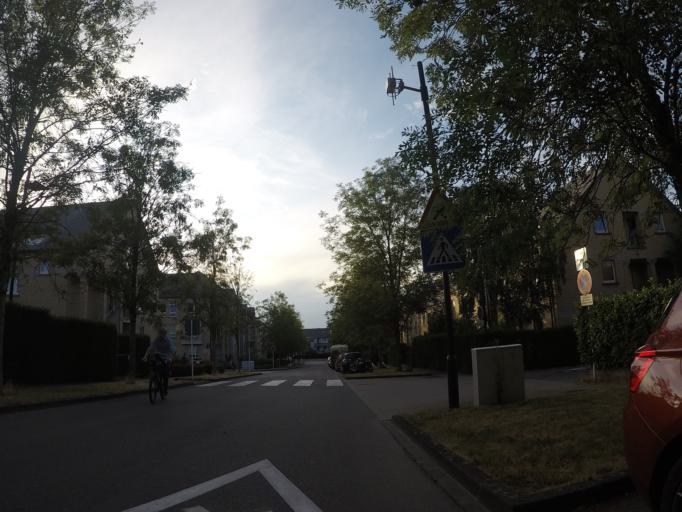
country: LU
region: Luxembourg
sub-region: Canton de Luxembourg
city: Luxembourg
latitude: 49.5925
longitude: 6.1269
